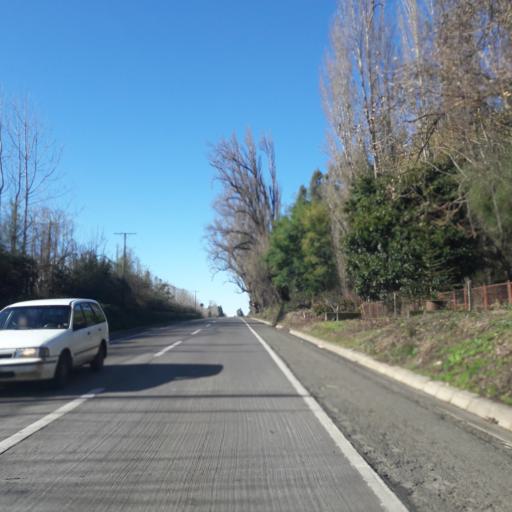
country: CL
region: Araucania
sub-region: Provincia de Malleco
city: Angol
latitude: -37.7517
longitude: -72.5862
